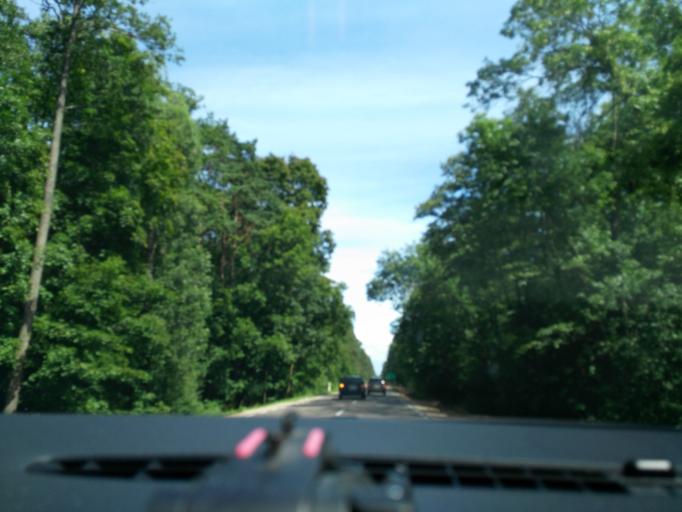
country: PL
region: Podlasie
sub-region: Powiat augustowski
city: Augustow
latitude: 53.8470
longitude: 23.0049
